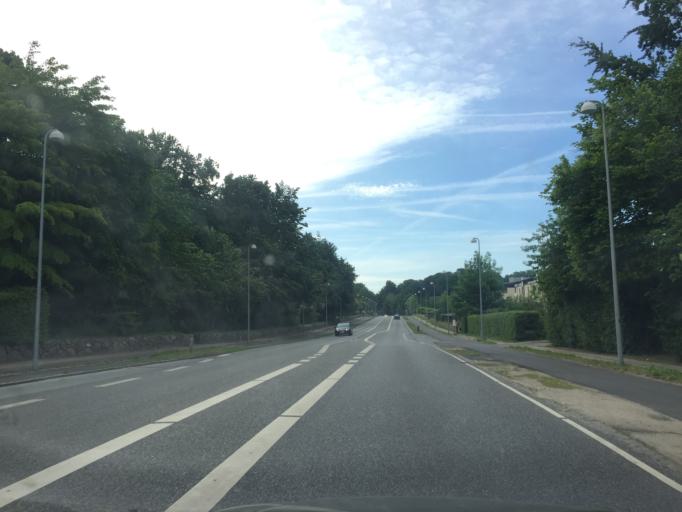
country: DK
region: Capital Region
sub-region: Lyngby-Tarbaek Kommune
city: Kongens Lyngby
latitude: 55.7821
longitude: 12.4917
